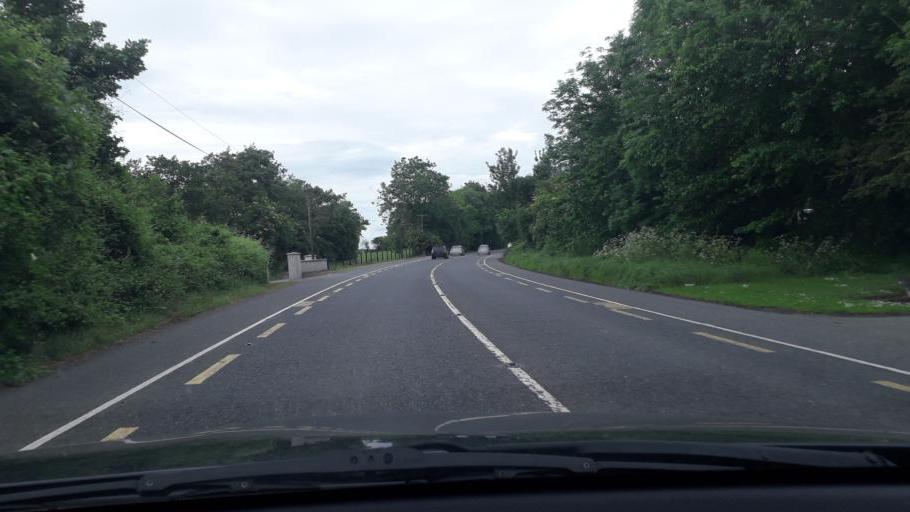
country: IE
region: Leinster
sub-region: County Carlow
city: Carlow
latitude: 52.7792
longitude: -6.9526
